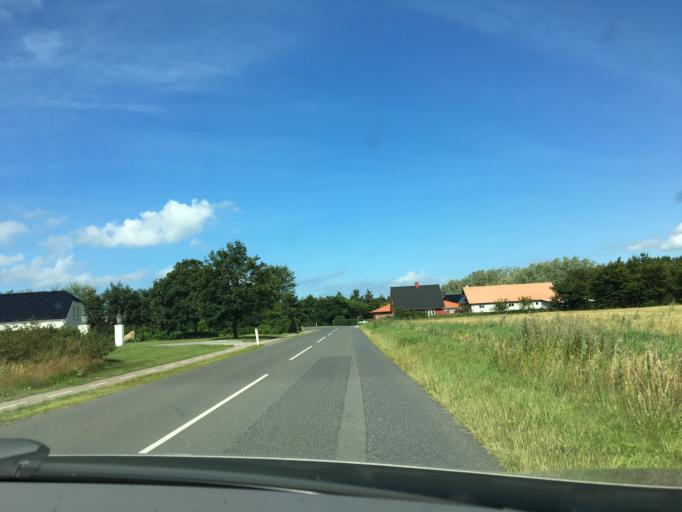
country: DK
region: Central Jutland
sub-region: Ringkobing-Skjern Kommune
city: Skjern
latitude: 55.9537
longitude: 8.4000
